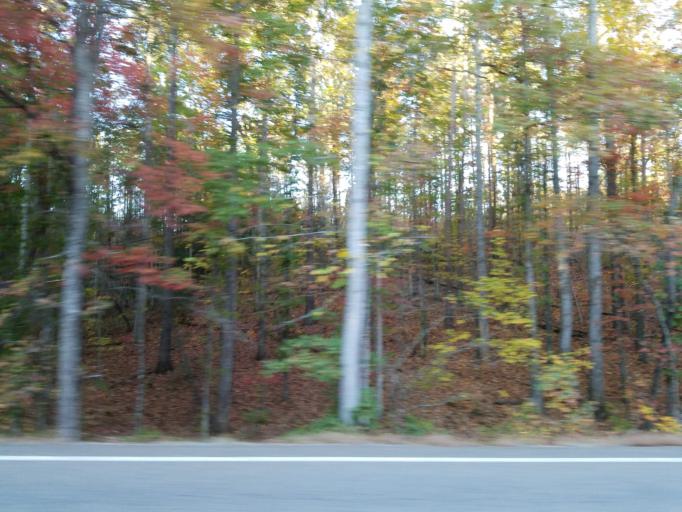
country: US
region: Georgia
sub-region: Dawson County
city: Dawsonville
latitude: 34.5459
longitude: -84.2252
